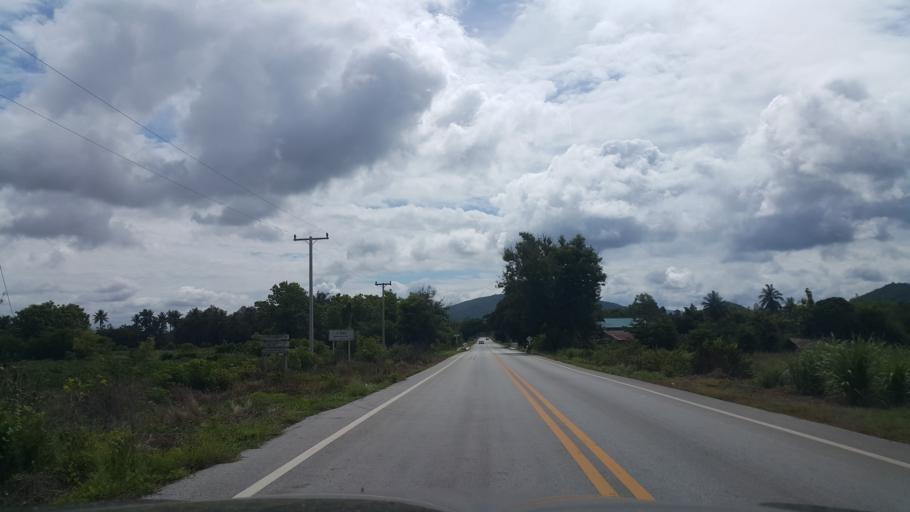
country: TH
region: Uttaradit
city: Thong Saen Khan
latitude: 17.3939
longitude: 100.2957
